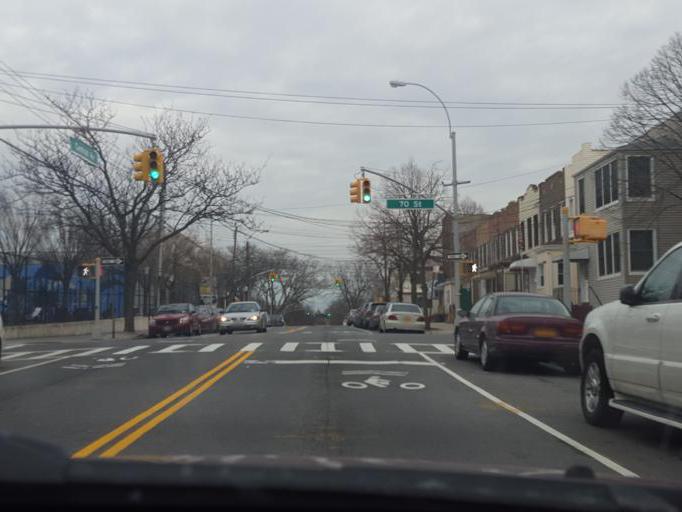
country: US
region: New York
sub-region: Kings County
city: East New York
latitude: 40.7043
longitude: -73.8821
